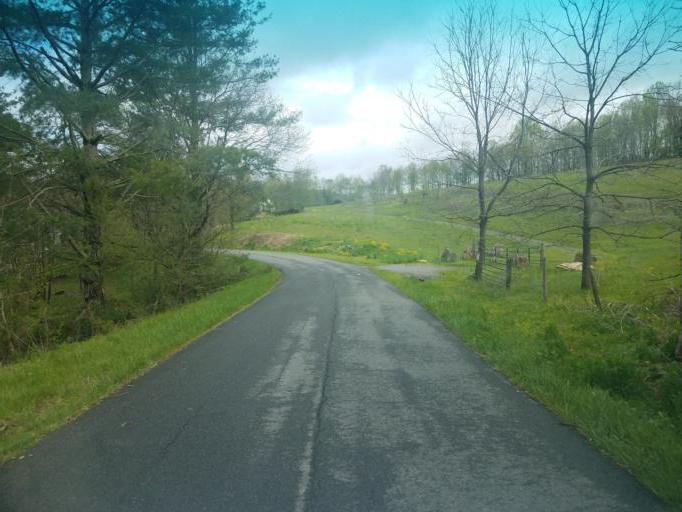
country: US
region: Virginia
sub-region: Smyth County
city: Atkins
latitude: 36.9729
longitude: -81.3912
